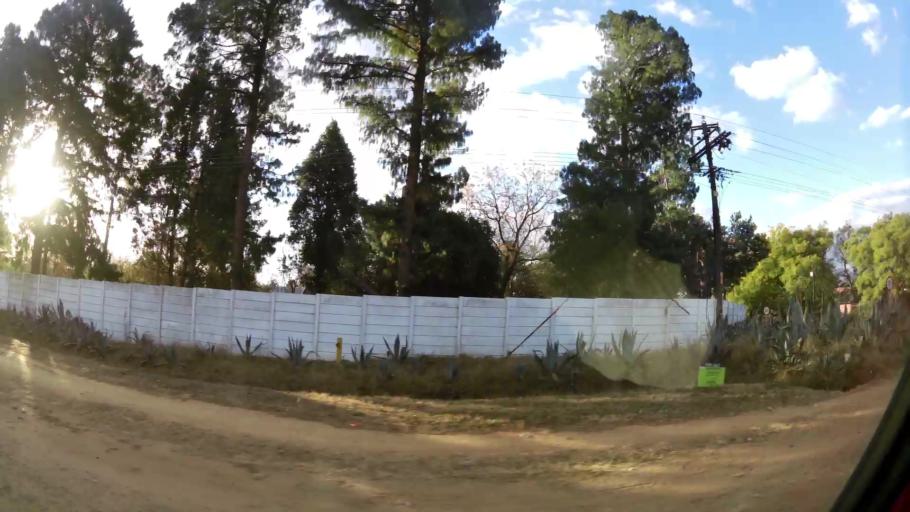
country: ZA
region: Gauteng
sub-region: City of Johannesburg Metropolitan Municipality
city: Midrand
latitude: -25.9569
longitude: 28.1689
